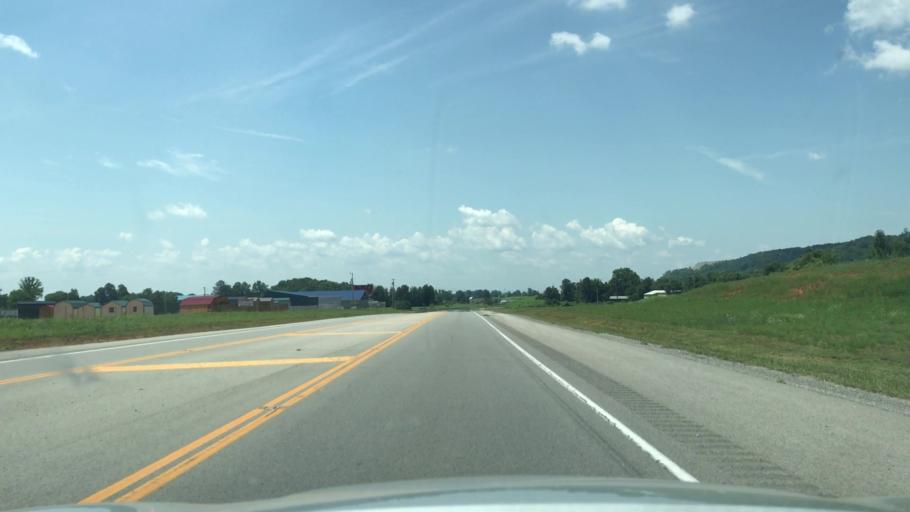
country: US
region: Kentucky
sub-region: Clinton County
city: Albany
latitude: 36.7248
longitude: -85.1376
